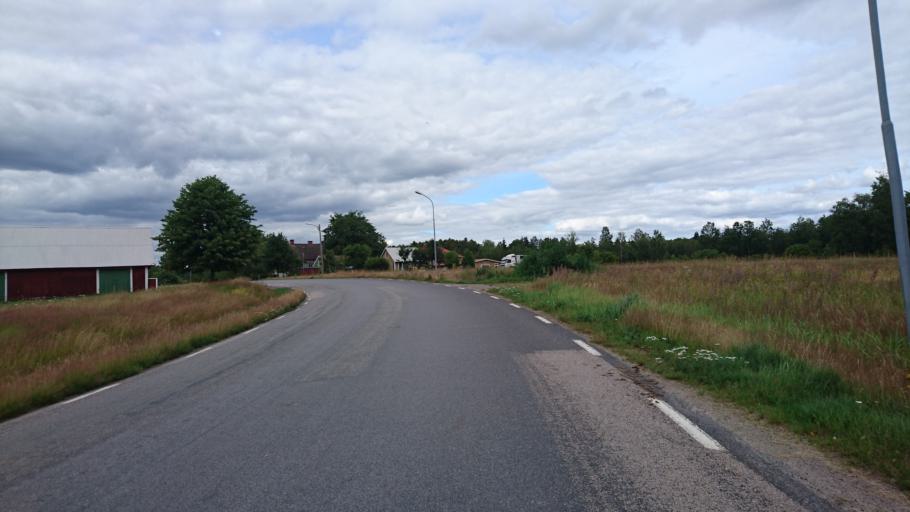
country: SE
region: Kronoberg
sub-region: Alvesta Kommun
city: Moheda
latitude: 56.9863
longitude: 14.5857
